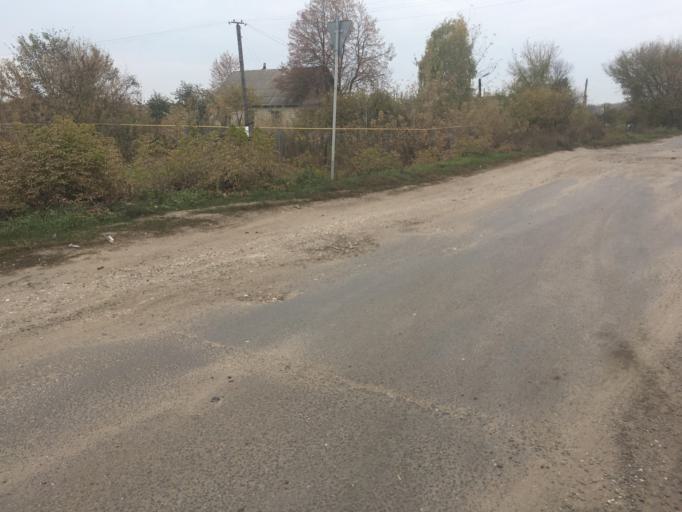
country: RU
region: Kursk
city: Kshenskiy
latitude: 51.8573
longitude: 37.7011
